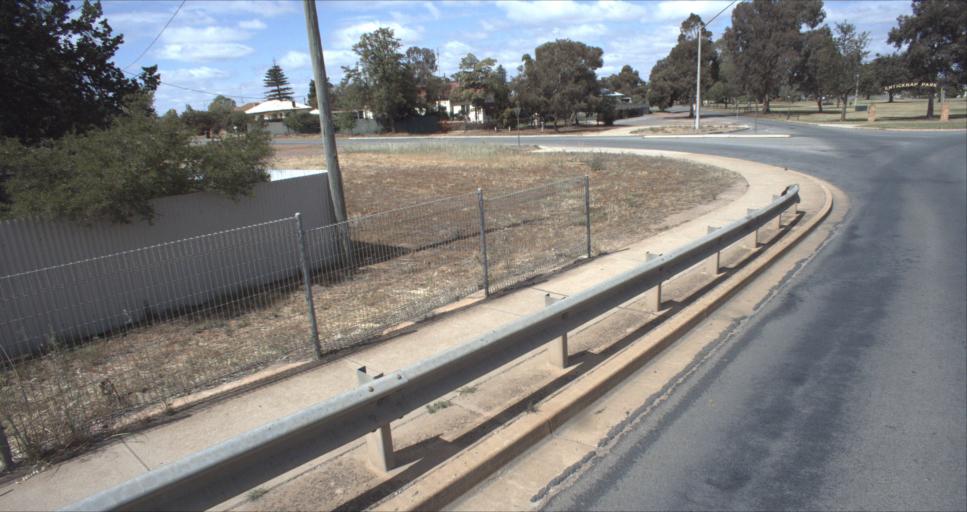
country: AU
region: New South Wales
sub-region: Leeton
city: Leeton
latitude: -34.5566
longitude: 146.4005
